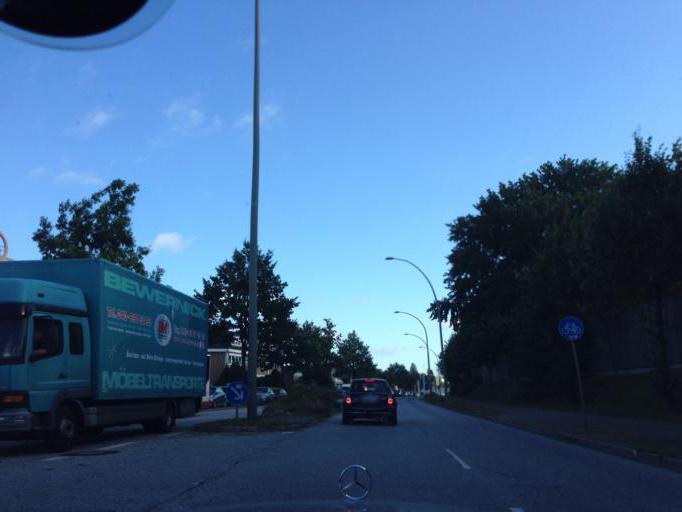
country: DE
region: Hamburg
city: Farmsen-Berne
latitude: 53.6009
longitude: 10.1141
